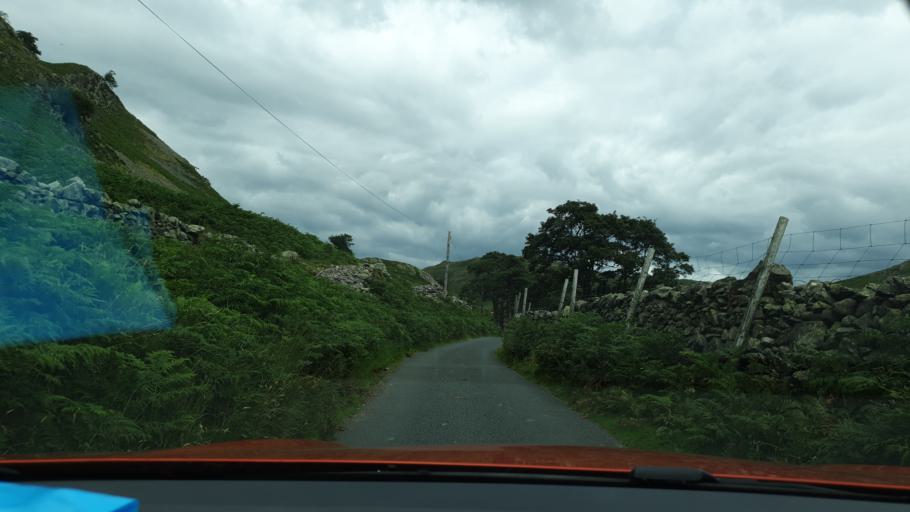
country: GB
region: England
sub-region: Cumbria
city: Ambleside
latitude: 54.5548
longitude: -2.8791
